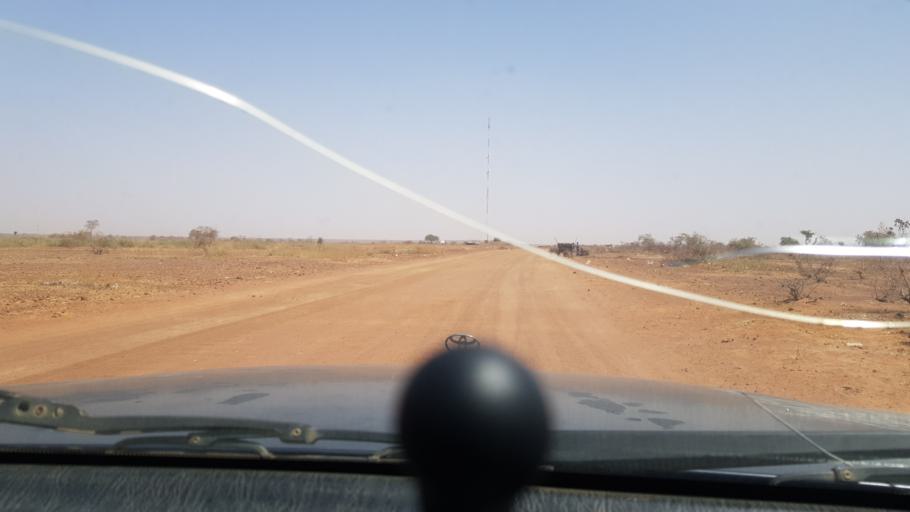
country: NE
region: Niamey
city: Niamey
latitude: 13.4285
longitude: 1.9742
